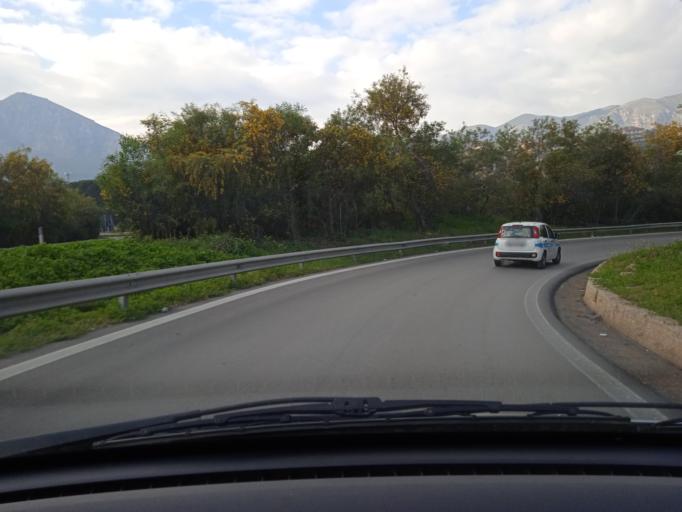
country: IT
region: Sicily
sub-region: Palermo
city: Villabate
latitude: 38.0820
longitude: 13.4398
